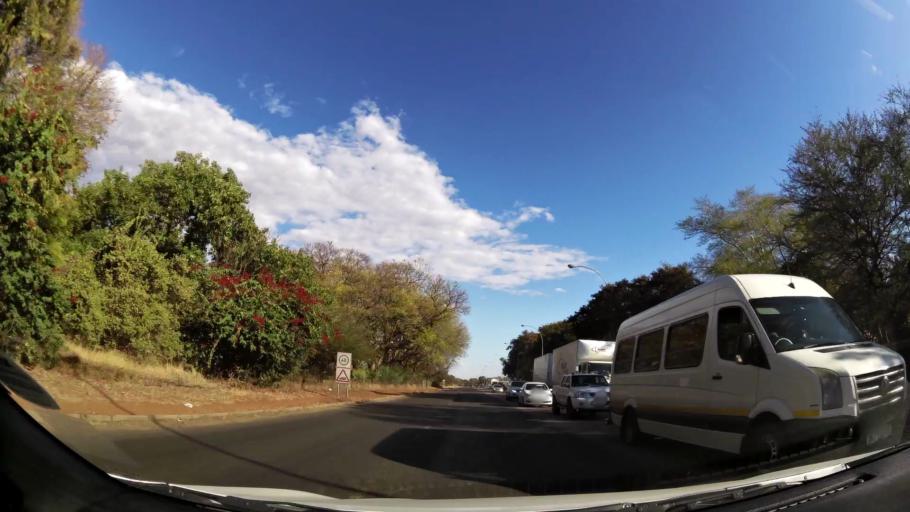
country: ZA
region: Limpopo
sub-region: Waterberg District Municipality
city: Mokopane
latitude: -24.1948
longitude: 29.0088
